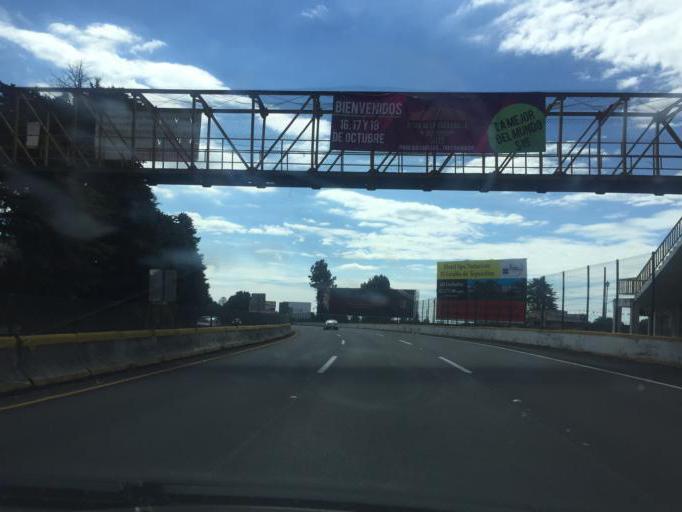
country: MX
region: Morelos
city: Tres Marias
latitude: 19.0497
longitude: -99.2407
